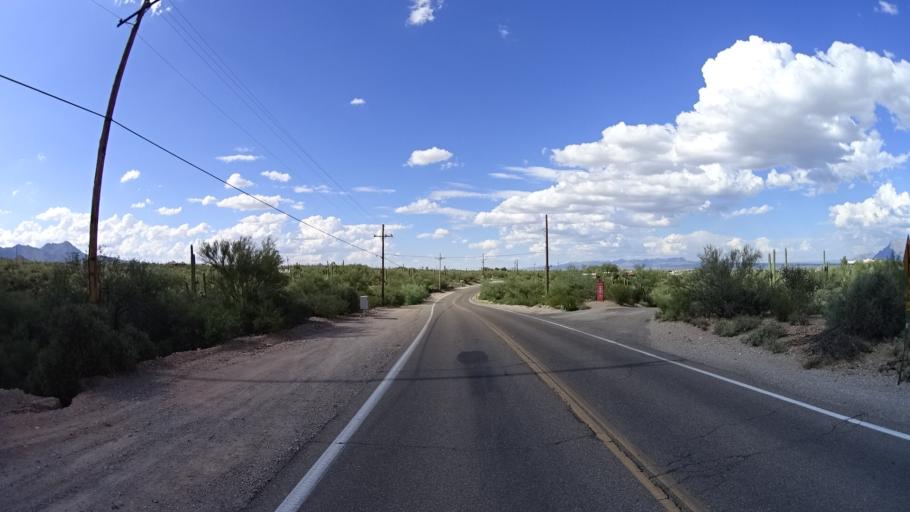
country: US
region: Arizona
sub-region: Pima County
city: Flowing Wells
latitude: 32.2587
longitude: -111.0623
